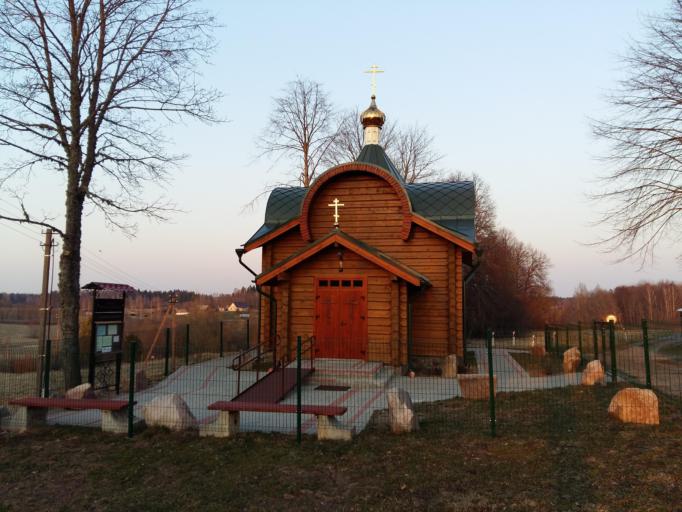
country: LT
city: Zarasai
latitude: 55.6592
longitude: 26.0708
